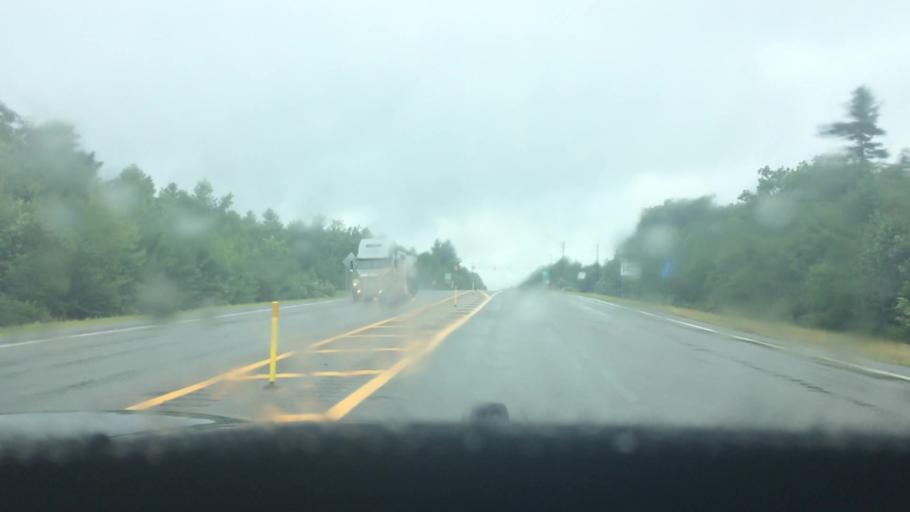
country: US
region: Massachusetts
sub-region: Worcester County
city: South Ashburnham
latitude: 42.5895
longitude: -71.9594
